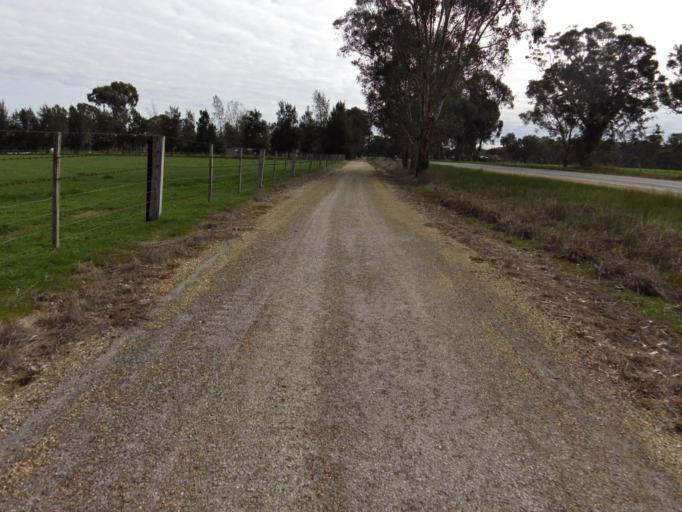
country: AU
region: Victoria
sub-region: Wangaratta
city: Wangaratta
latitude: -36.4029
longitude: 146.3477
